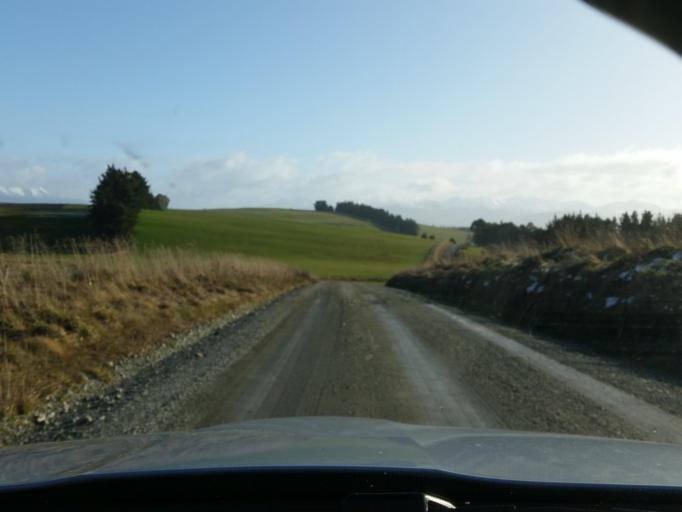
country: NZ
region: Southland
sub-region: Southland District
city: Te Anau
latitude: -45.4620
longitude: 167.8329
